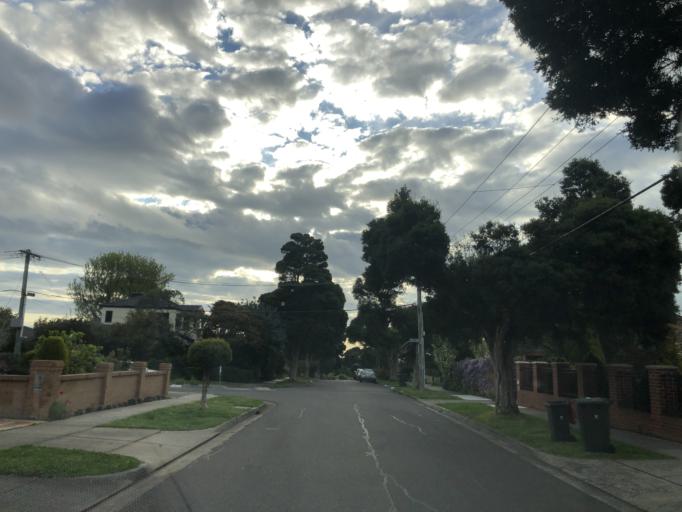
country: AU
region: Victoria
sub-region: Whitehorse
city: Burwood
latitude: -37.8622
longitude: 145.1232
